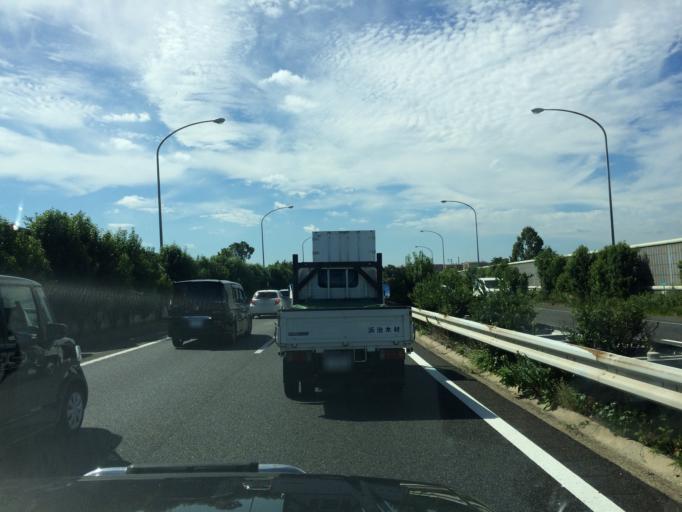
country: JP
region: Osaka
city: Takaishi
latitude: 34.5033
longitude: 135.4888
